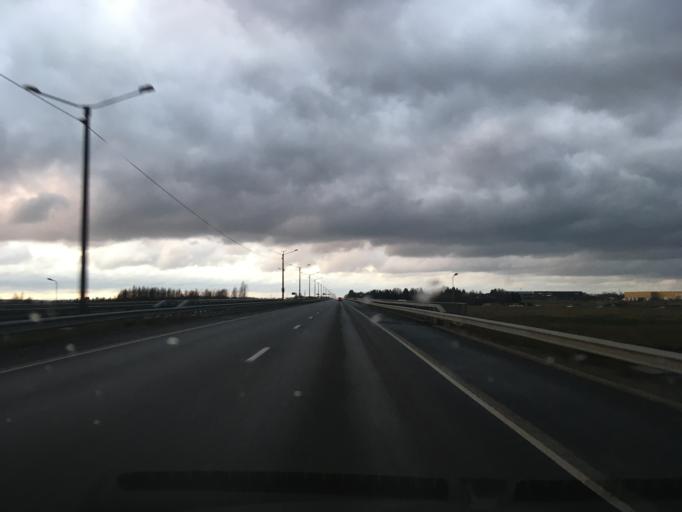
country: EE
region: Harju
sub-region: Rae vald
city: Jueri
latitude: 59.3515
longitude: 24.8853
